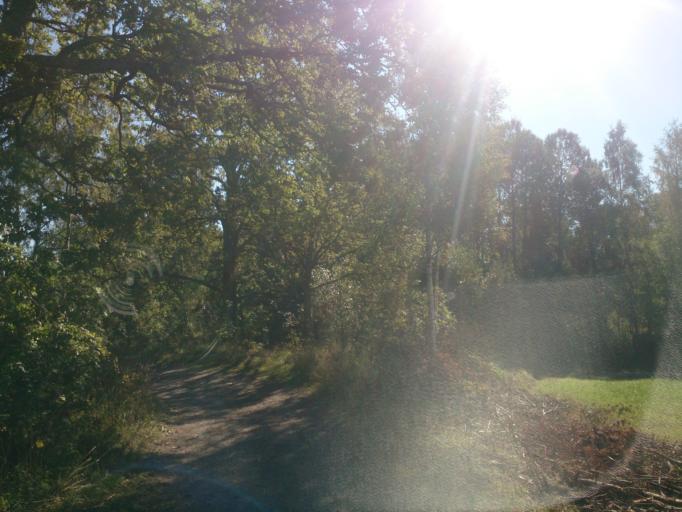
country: SE
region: OEstergoetland
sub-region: Atvidabergs Kommun
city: Atvidaberg
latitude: 58.2210
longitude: 15.9769
